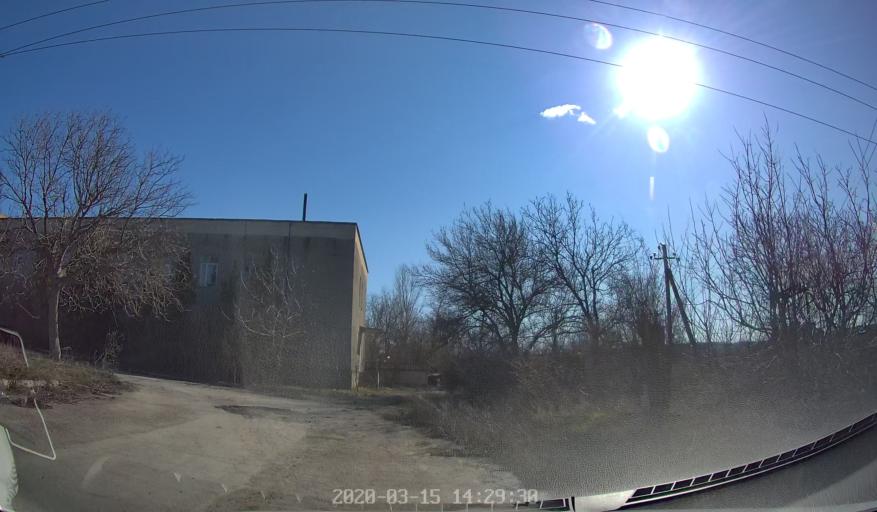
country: MD
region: Orhei
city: Orhei
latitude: 47.3466
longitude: 28.8855
